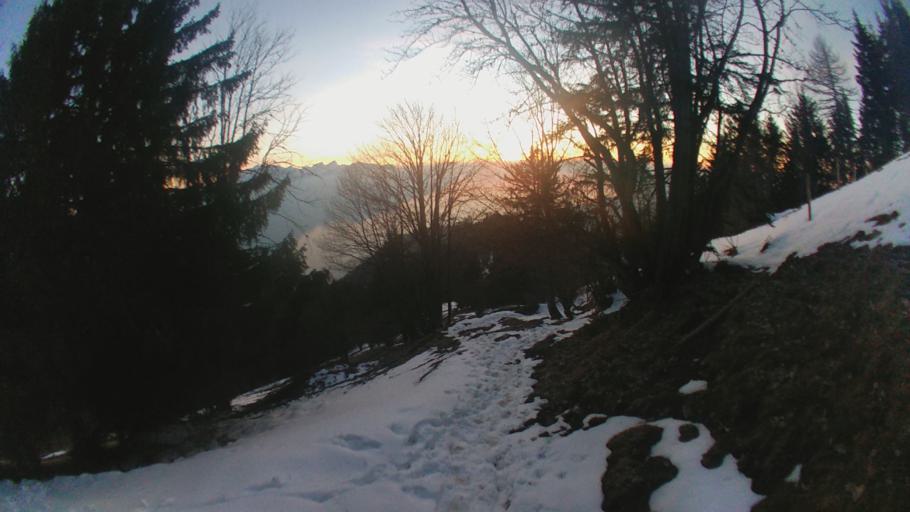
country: CH
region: Vaud
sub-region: Riviera-Pays-d'Enhaut District
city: Caux
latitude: 46.4353
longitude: 6.9593
